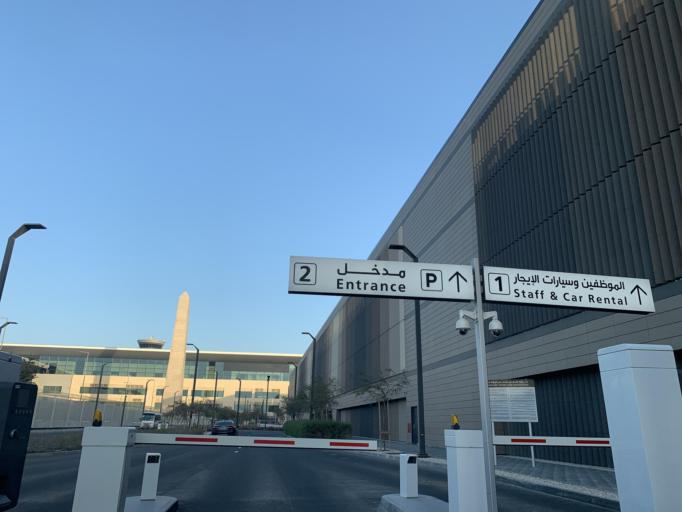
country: BH
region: Muharraq
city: Al Muharraq
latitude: 26.2680
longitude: 50.6275
